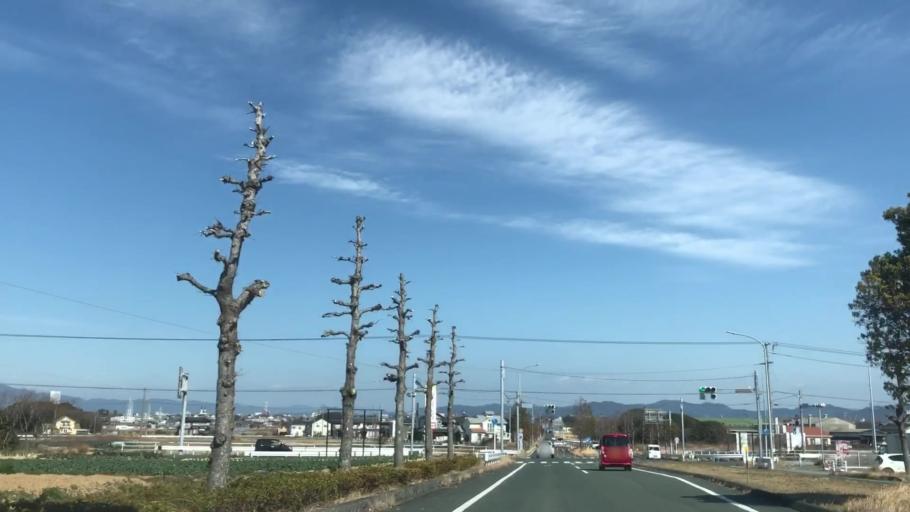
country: JP
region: Aichi
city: Toyohashi
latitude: 34.7121
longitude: 137.3594
